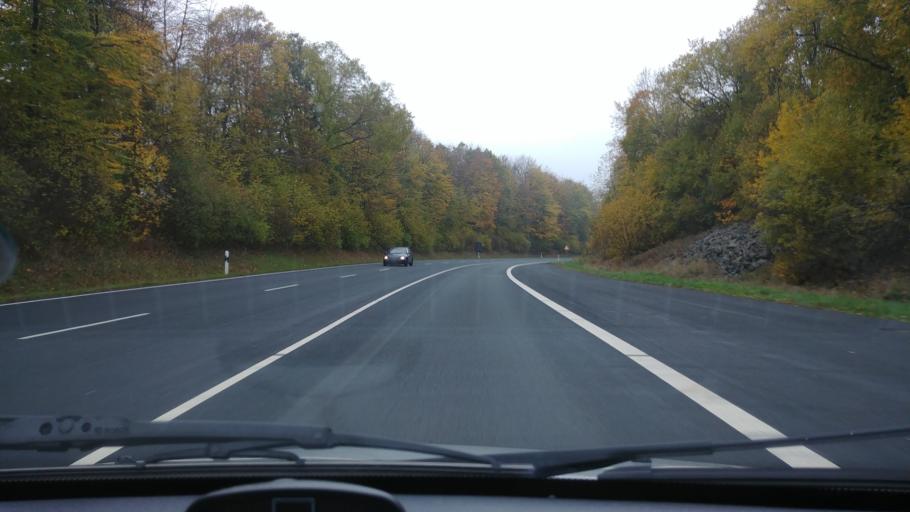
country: DE
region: Rheinland-Pfalz
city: Langenhahn
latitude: 50.5897
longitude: 7.9157
